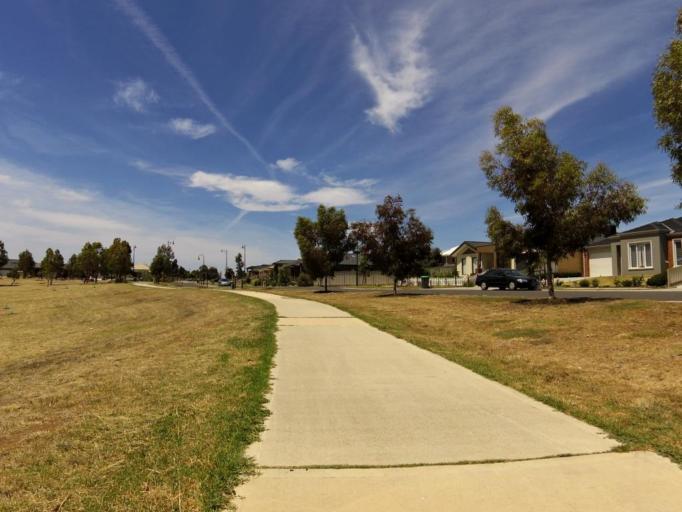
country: AU
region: Victoria
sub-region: Wyndham
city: Williams Landing
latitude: -37.8637
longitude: 144.7212
